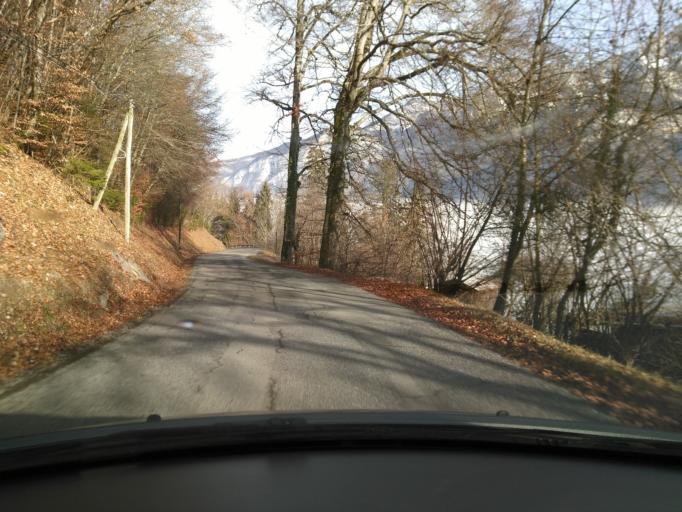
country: FR
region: Rhone-Alpes
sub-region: Departement de la Haute-Savoie
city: Sallanches
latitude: 45.9653
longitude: 6.6129
